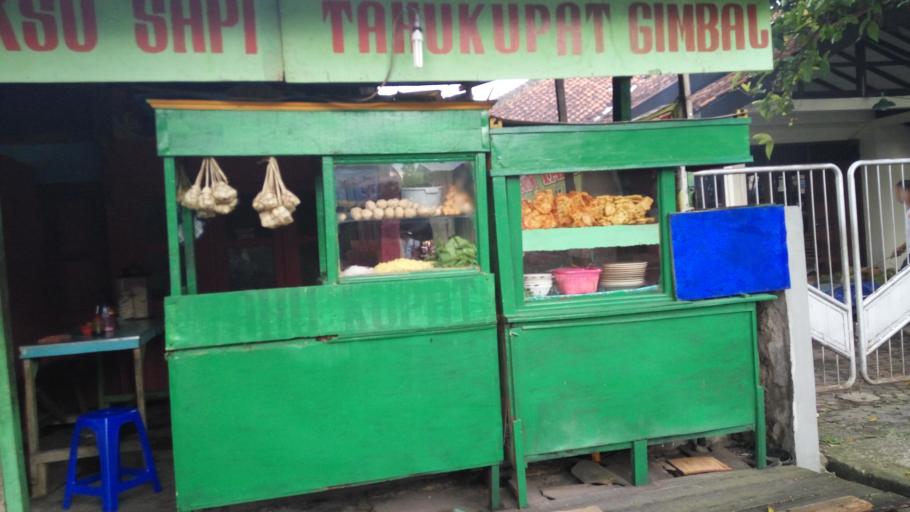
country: ID
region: Central Java
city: Ambarawa
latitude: -7.2721
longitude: 110.4025
